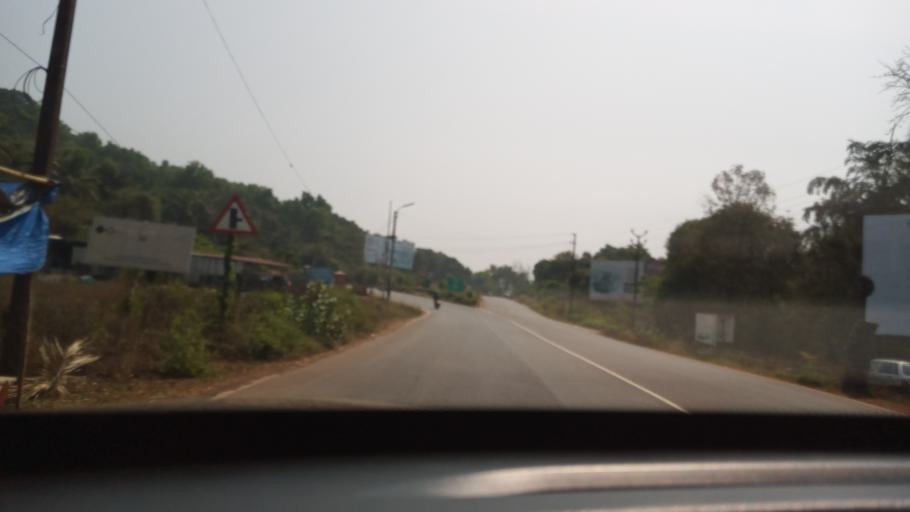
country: IN
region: Goa
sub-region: South Goa
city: Raia
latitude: 15.3305
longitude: 73.9298
